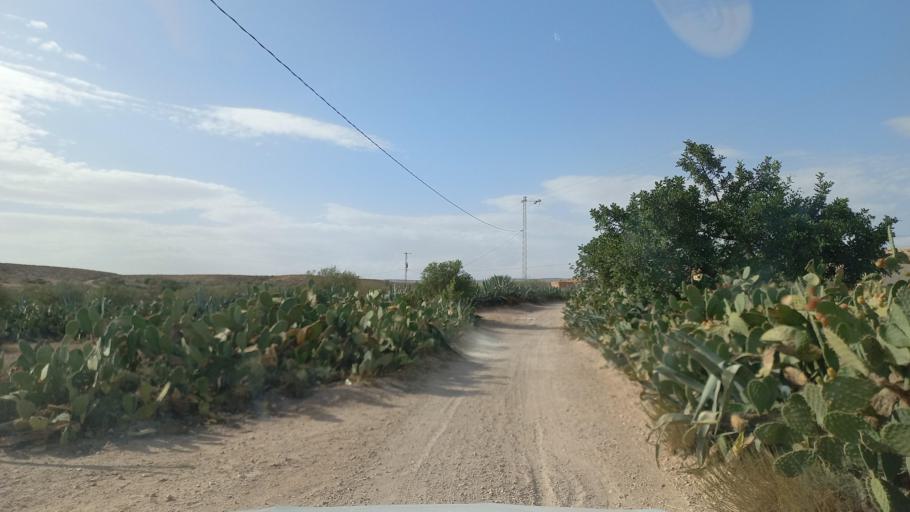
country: TN
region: Al Qasrayn
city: Kasserine
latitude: 35.2549
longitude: 8.9309
